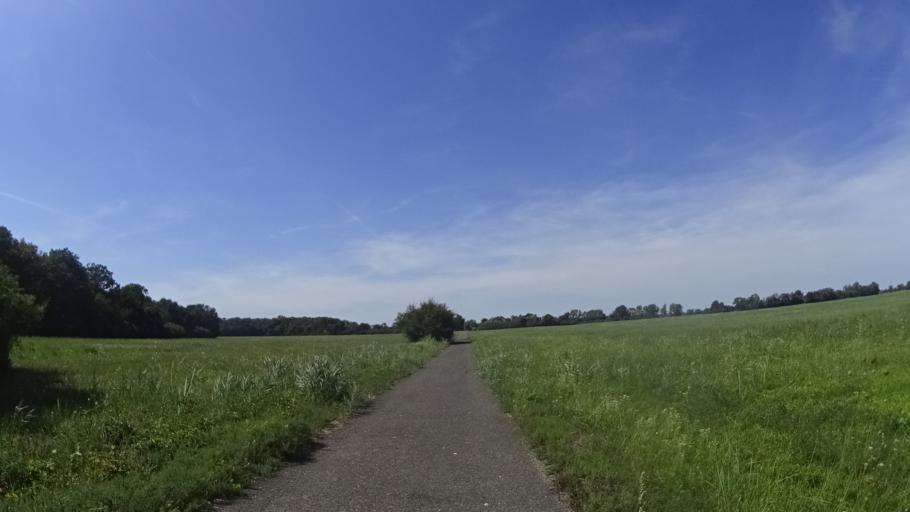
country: AT
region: Lower Austria
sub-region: Politischer Bezirk Ganserndorf
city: Angern an der March
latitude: 48.3579
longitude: 16.8790
